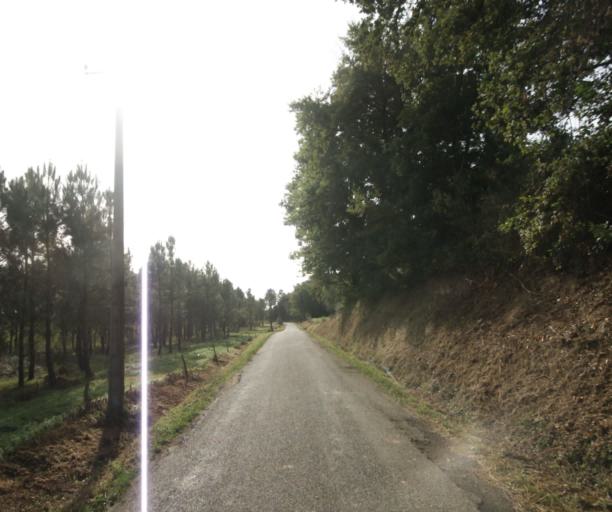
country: FR
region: Midi-Pyrenees
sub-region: Departement du Gers
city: Eauze
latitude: 43.9164
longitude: 0.1348
